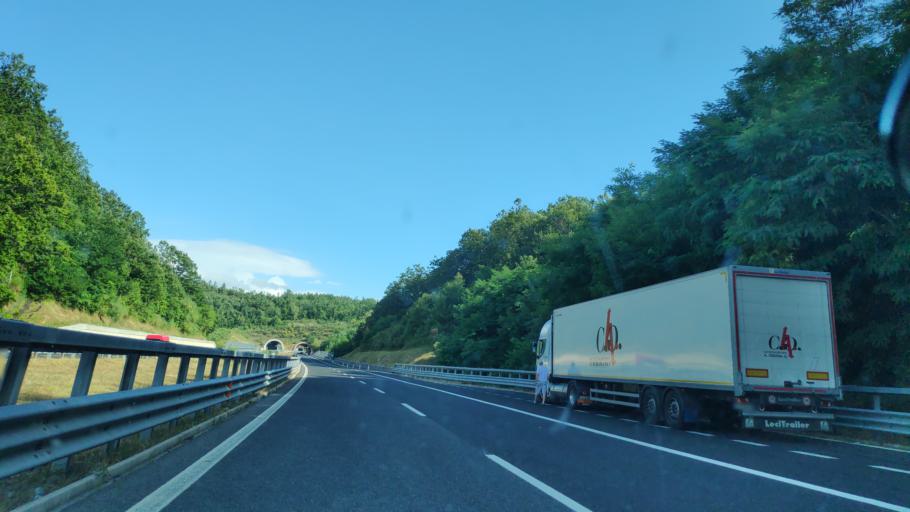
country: IT
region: Campania
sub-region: Provincia di Salerno
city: Casalbuono
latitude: 40.2374
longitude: 15.6609
